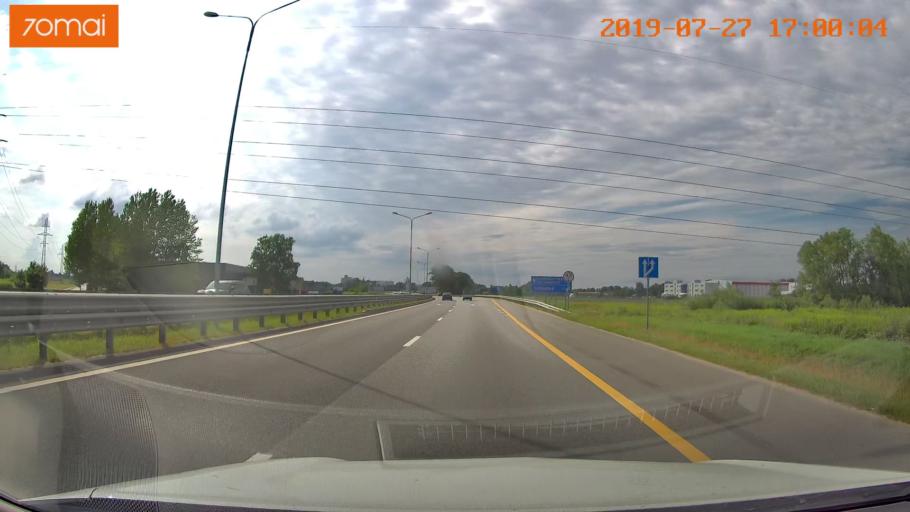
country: RU
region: Kaliningrad
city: Bol'shoe Isakovo
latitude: 54.7067
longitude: 20.6338
